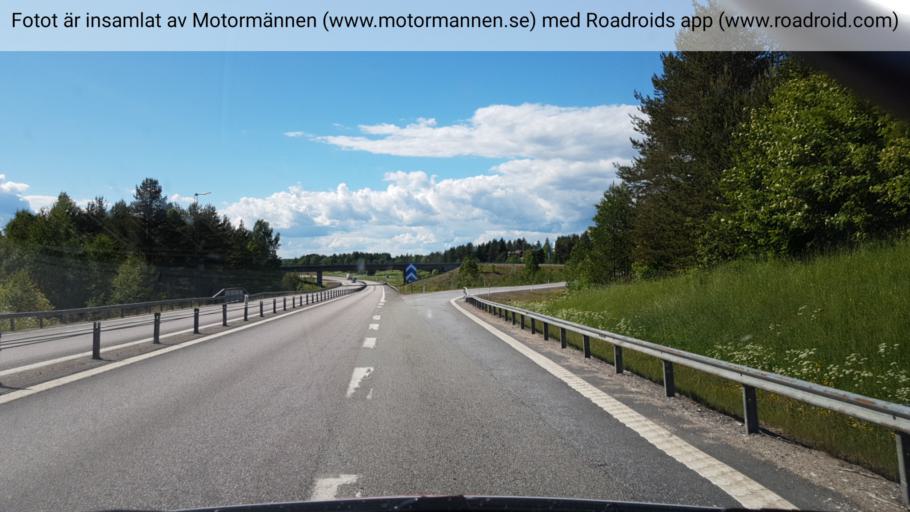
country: SE
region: Norrbotten
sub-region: Kalix Kommun
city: Toere
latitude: 65.9095
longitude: 22.6609
